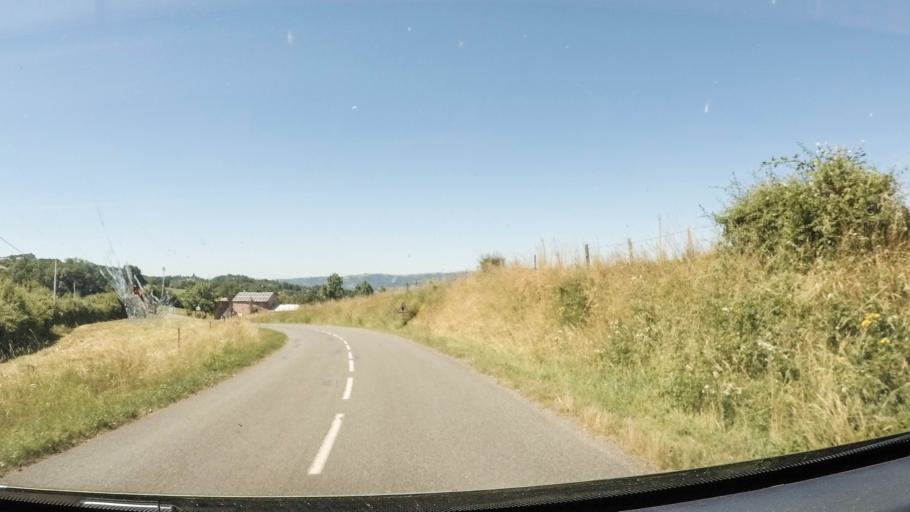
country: FR
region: Midi-Pyrenees
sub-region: Departement de l'Aveyron
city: Saint-Christophe-Vallon
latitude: 44.4823
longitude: 2.3446
